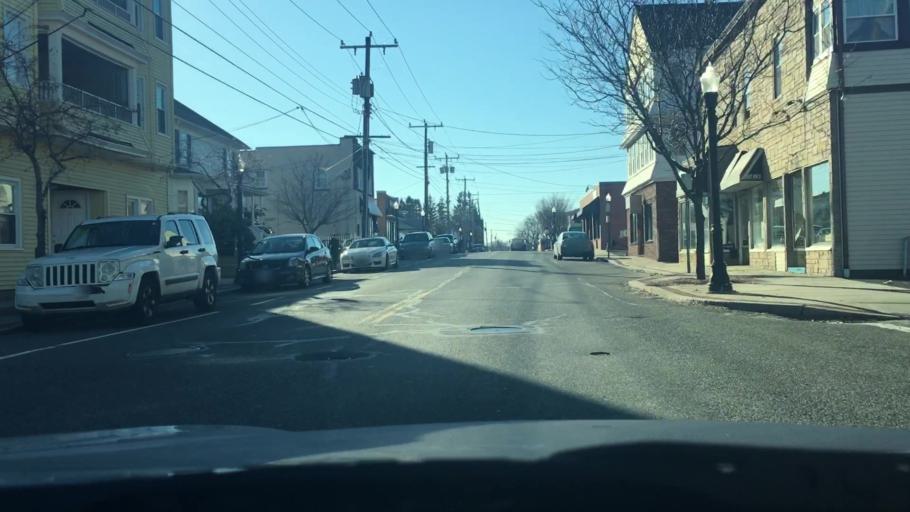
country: US
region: Massachusetts
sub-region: Hampden County
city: Ludlow
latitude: 42.1591
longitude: -72.4746
